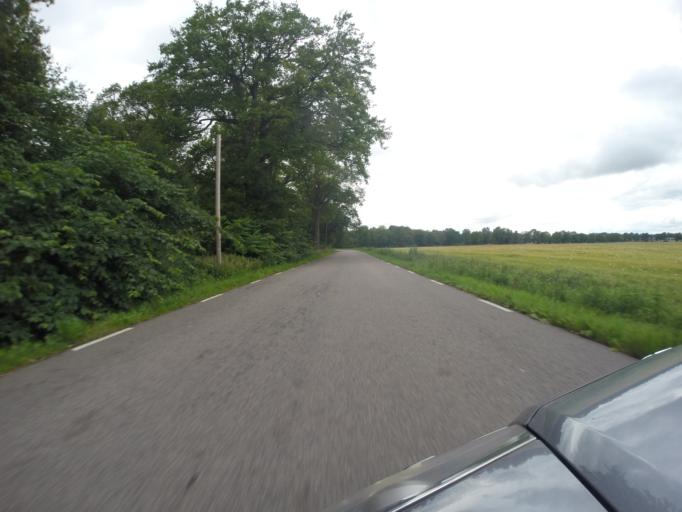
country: SE
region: Skane
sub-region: Helsingborg
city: Hyllinge
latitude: 56.0791
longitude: 12.8332
